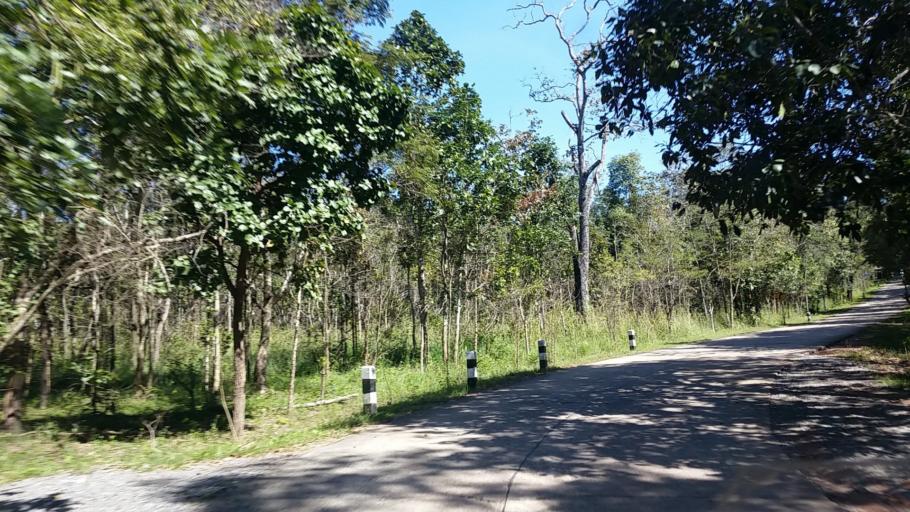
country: TH
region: Chaiyaphum
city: Sap Yai
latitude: 15.6355
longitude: 101.3932
